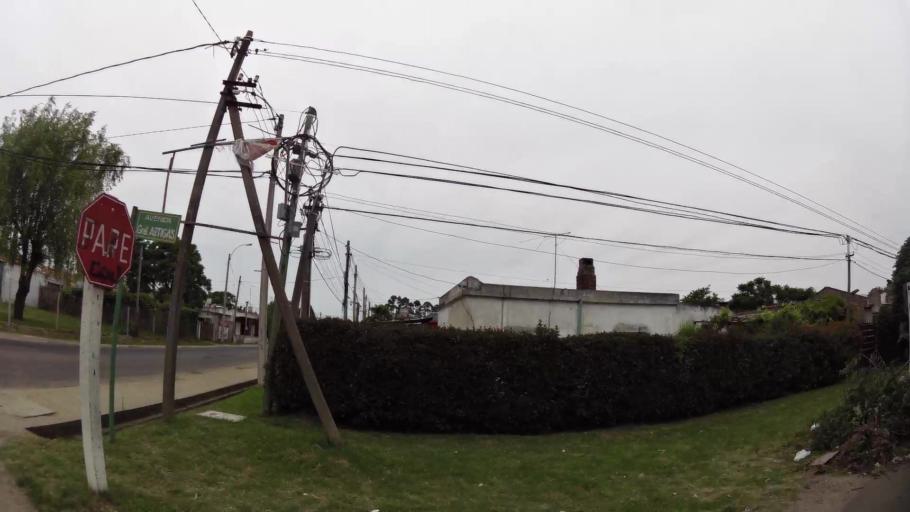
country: UY
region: Canelones
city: Las Piedras
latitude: -34.7274
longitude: -56.2277
